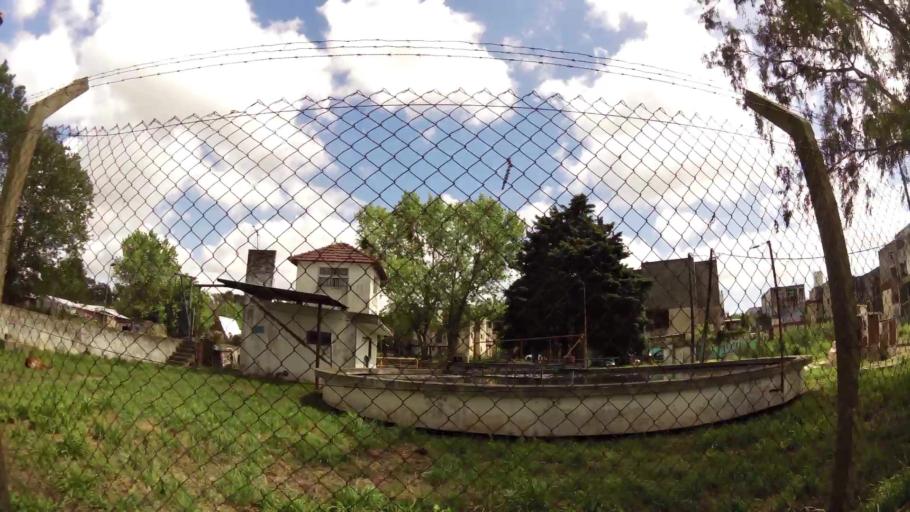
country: AR
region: Buenos Aires
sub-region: Partido de Quilmes
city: Quilmes
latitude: -34.8349
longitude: -58.2219
